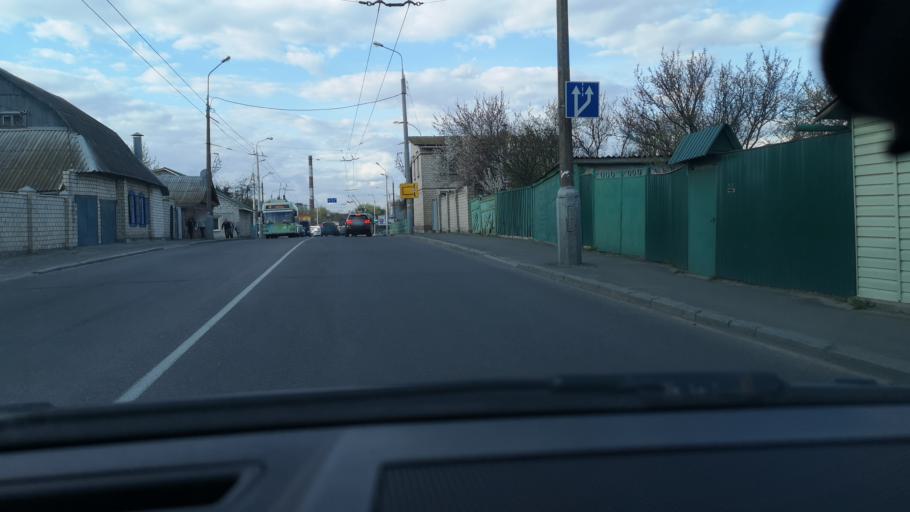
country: BY
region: Gomel
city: Gomel
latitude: 52.4384
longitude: 30.9775
